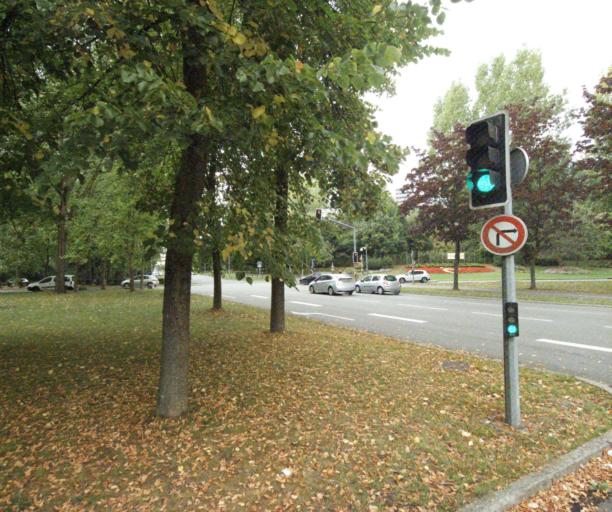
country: FR
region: Nord-Pas-de-Calais
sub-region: Departement du Nord
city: La Madeleine
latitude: 50.6485
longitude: 3.0692
